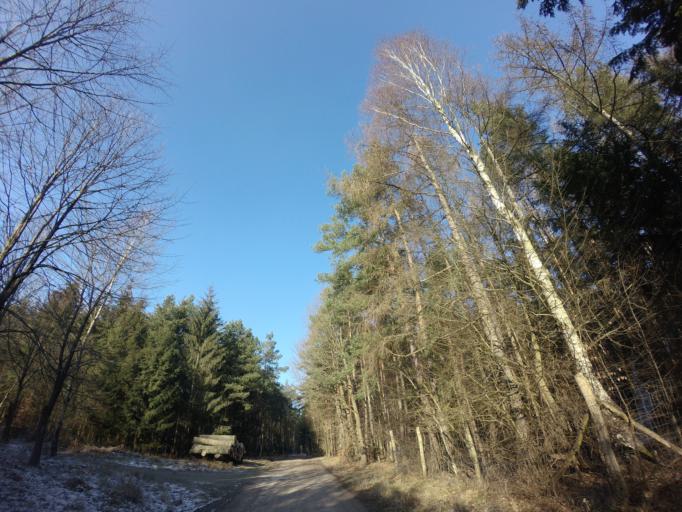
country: PL
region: West Pomeranian Voivodeship
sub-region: Powiat choszczenski
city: Pelczyce
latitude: 52.9544
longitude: 15.3326
